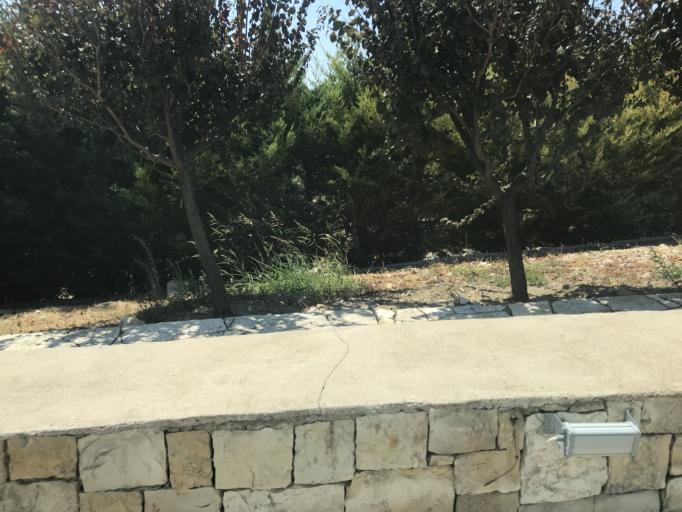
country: TR
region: Izmir
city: Urla
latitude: 38.2522
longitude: 26.7366
